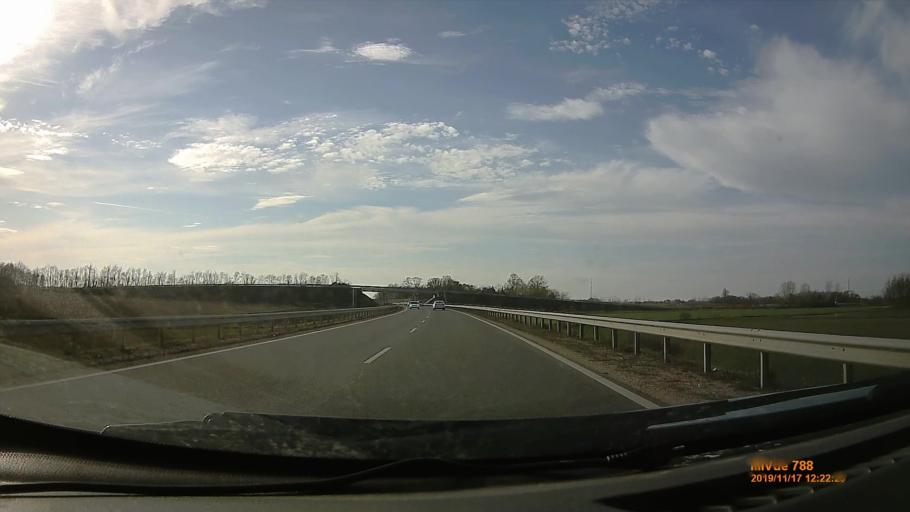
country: HU
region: Bacs-Kiskun
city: Kecskemet
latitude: 46.9498
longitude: 19.6736
